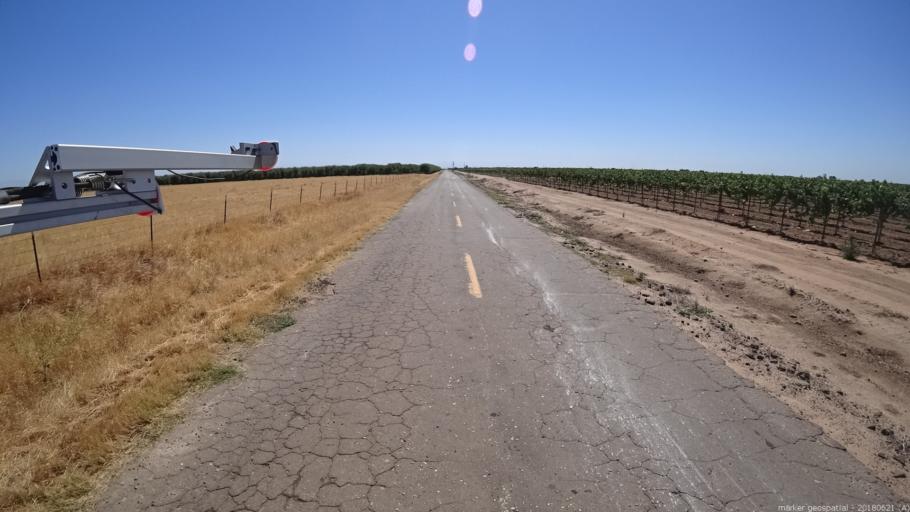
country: US
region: California
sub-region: Madera County
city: Parksdale
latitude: 36.9095
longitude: -119.9530
